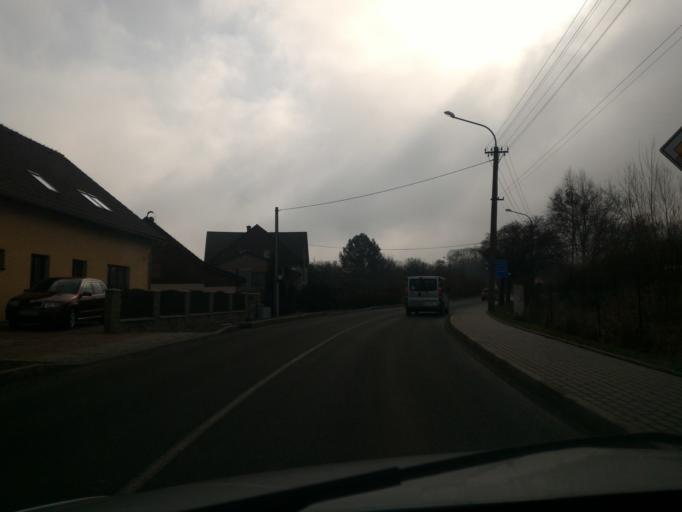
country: CZ
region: Liberecky
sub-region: Okres Liberec
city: Raspenava
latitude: 50.9049
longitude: 15.1139
